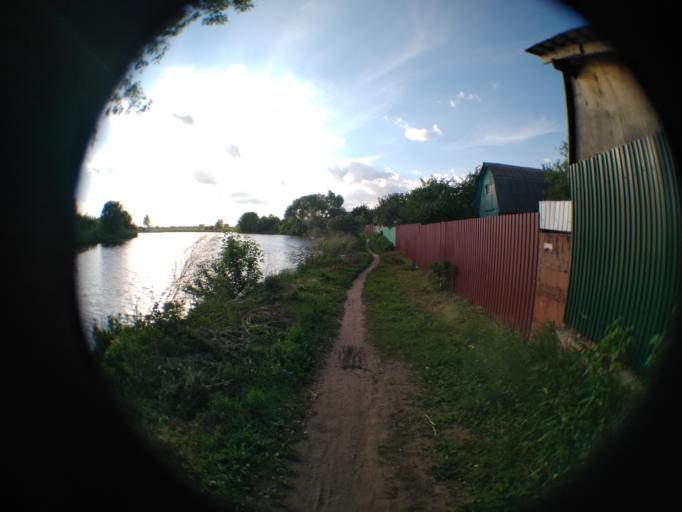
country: RU
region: Moskovskaya
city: Zhukovskiy
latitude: 55.5817
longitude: 38.1029
